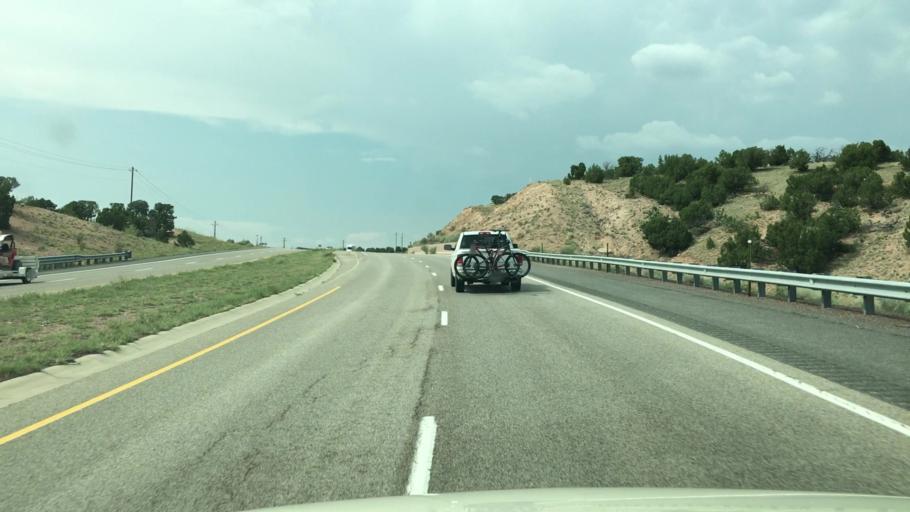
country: US
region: New Mexico
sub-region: Santa Fe County
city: Eldorado at Santa Fe
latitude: 35.4898
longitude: -105.9024
